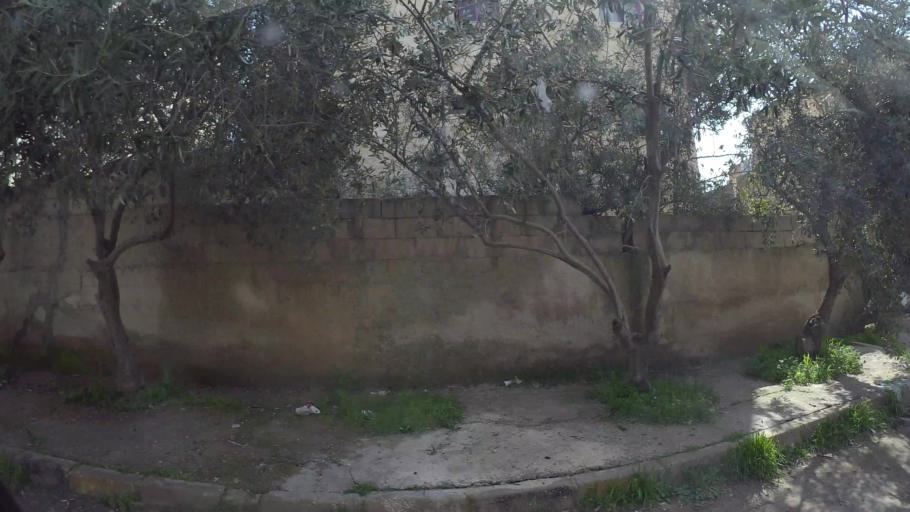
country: JO
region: Amman
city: Al Jubayhah
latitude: 32.0637
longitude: 35.8340
